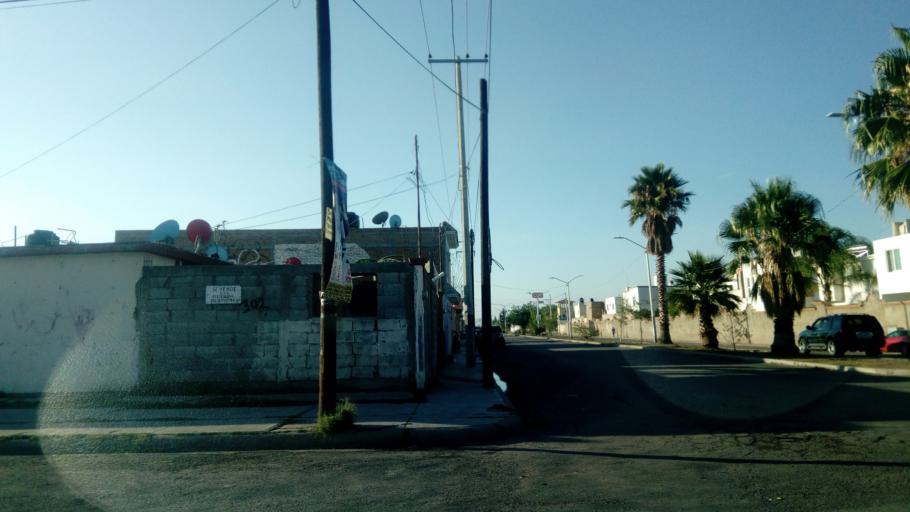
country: MX
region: Durango
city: Victoria de Durango
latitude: 24.0526
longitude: -104.6009
